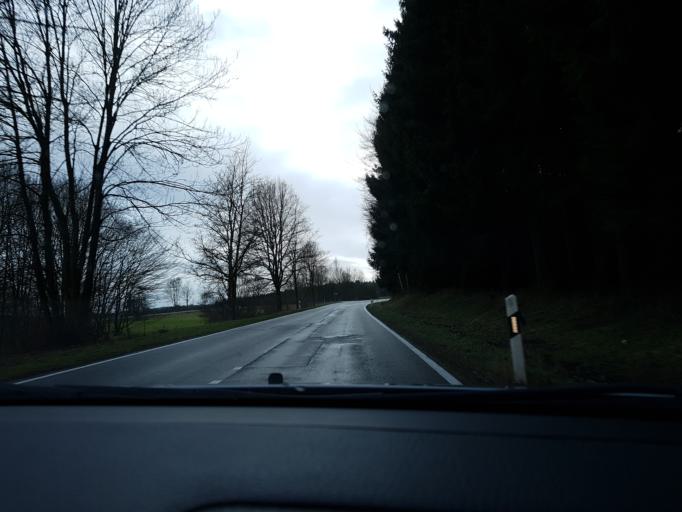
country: DE
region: Rheinland-Pfalz
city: Oberelbert
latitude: 50.3866
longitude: 7.8105
